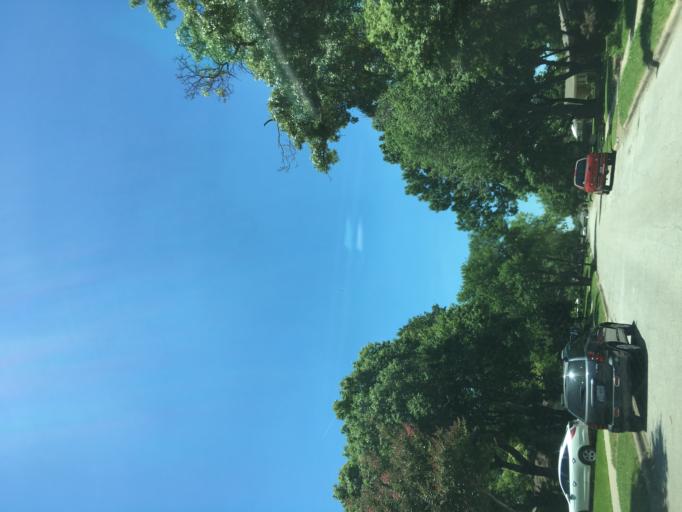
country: US
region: Texas
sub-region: Dallas County
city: Richardson
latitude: 32.9617
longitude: -96.7308
